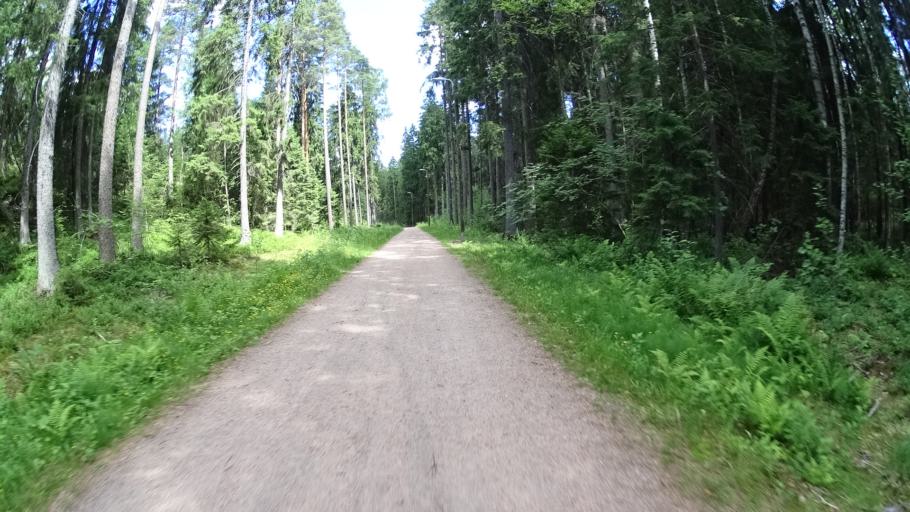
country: FI
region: Uusimaa
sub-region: Helsinki
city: Espoo
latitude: 60.2030
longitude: 24.6191
